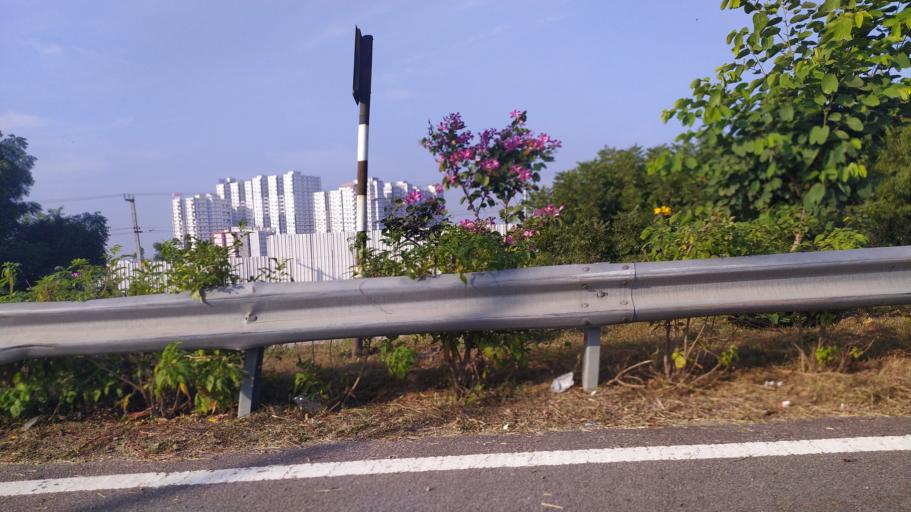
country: IN
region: Telangana
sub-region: Hyderabad
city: Hyderabad
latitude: 17.3951
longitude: 78.3487
